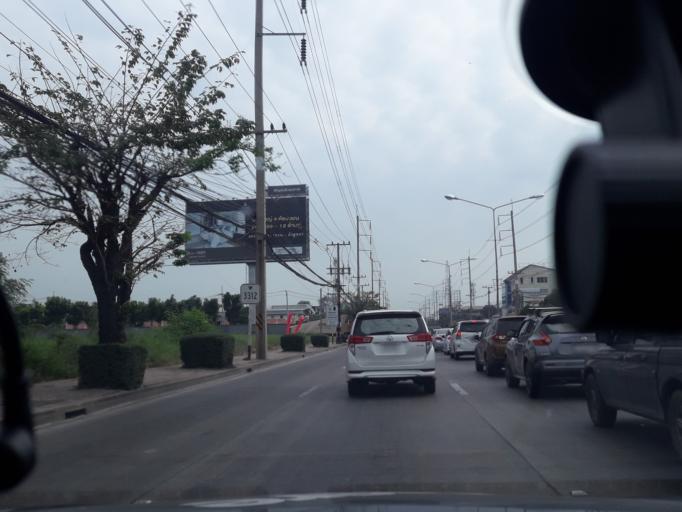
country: TH
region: Pathum Thani
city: Lam Luk Ka
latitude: 13.9348
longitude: 100.7418
